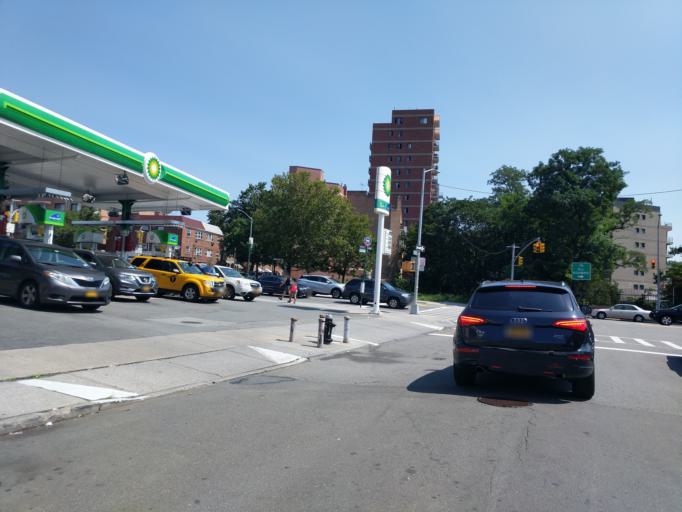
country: US
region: New York
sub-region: Queens County
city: Jamaica
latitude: 40.7519
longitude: -73.8327
